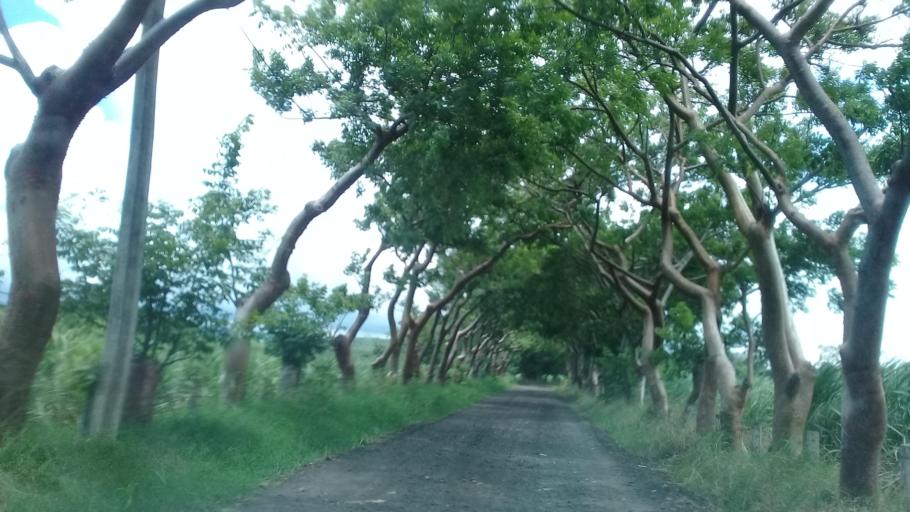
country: MX
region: Veracruz
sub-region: Naolinco
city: El Espinal
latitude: 19.5884
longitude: -96.8601
